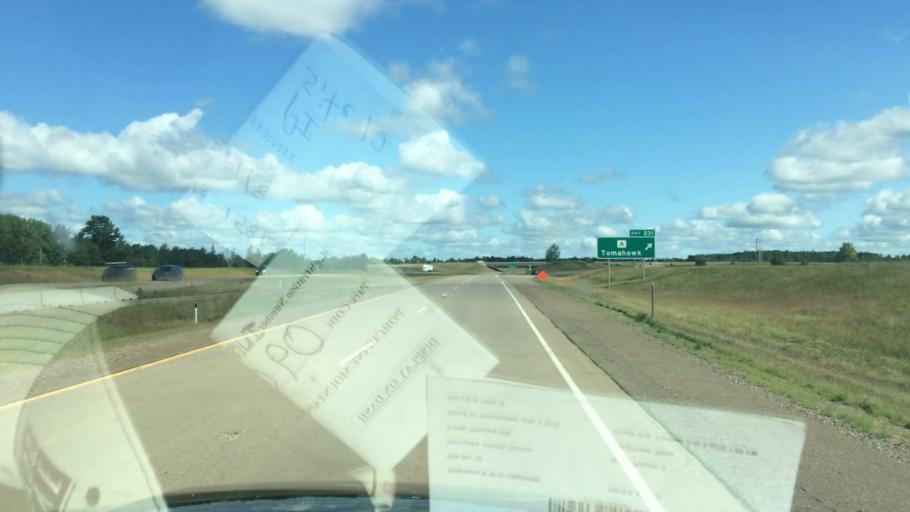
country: US
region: Wisconsin
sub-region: Lincoln County
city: Tomahawk
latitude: 45.4902
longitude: -89.6953
